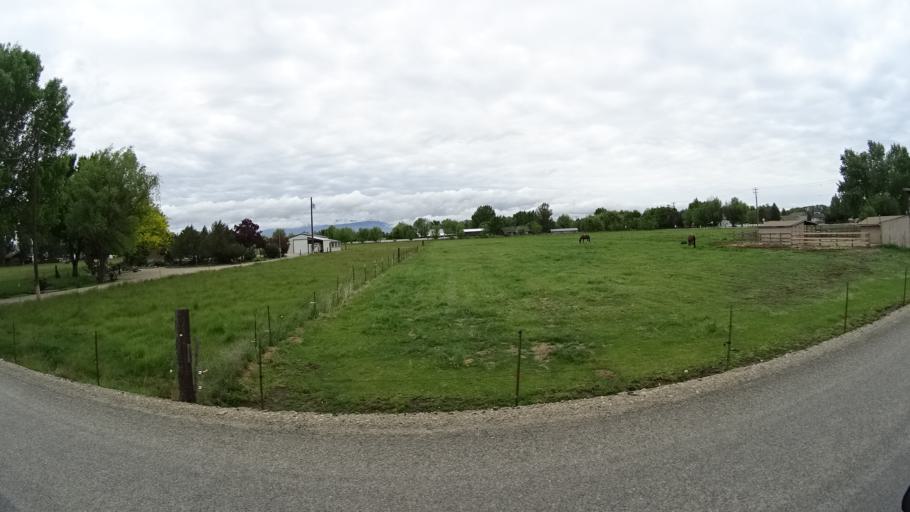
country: US
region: Idaho
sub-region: Ada County
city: Eagle
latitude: 43.7221
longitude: -116.4136
